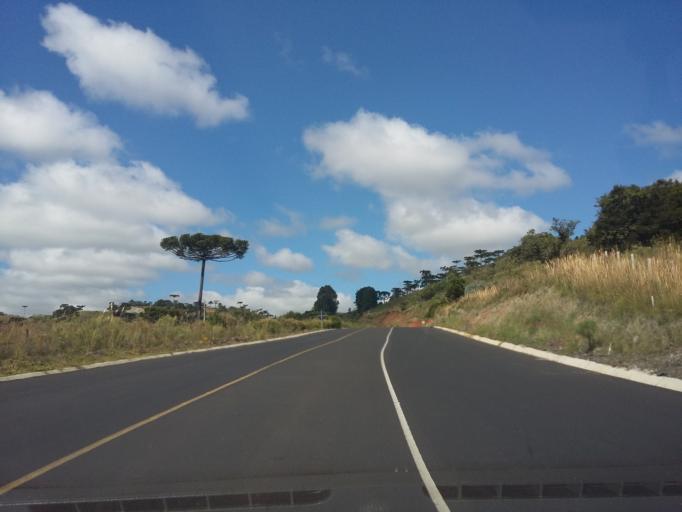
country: BR
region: Santa Catarina
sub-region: Sao Joaquim
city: Sao Joaquim
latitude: -28.1016
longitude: -50.0510
